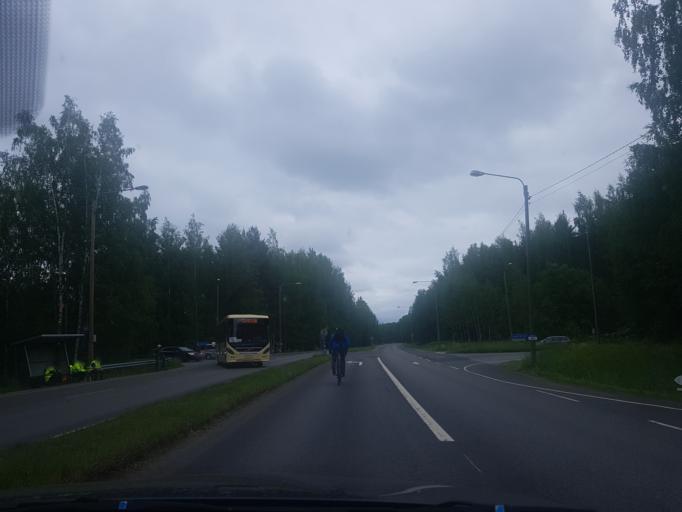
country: FI
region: Pirkanmaa
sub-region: Tampere
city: Kangasala
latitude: 61.4088
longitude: 24.1630
